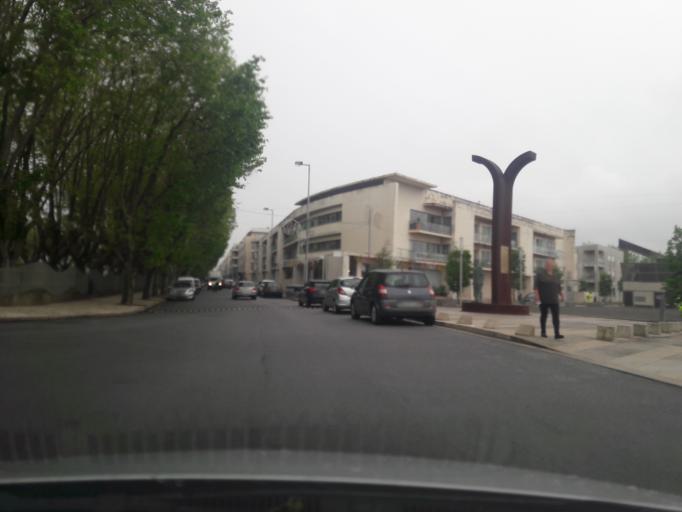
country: PT
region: Porto
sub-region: Vila do Conde
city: Vila do Conde
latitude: 41.3472
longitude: -8.7450
